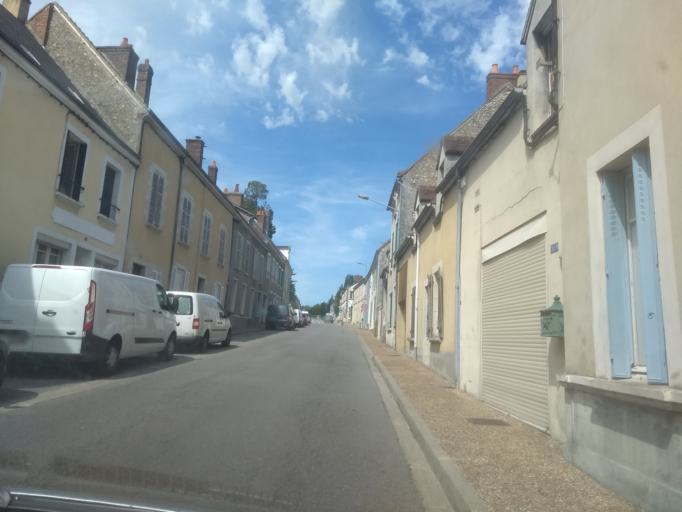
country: FR
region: Lower Normandy
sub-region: Departement de l'Orne
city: Remalard
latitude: 48.4293
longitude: 0.7733
